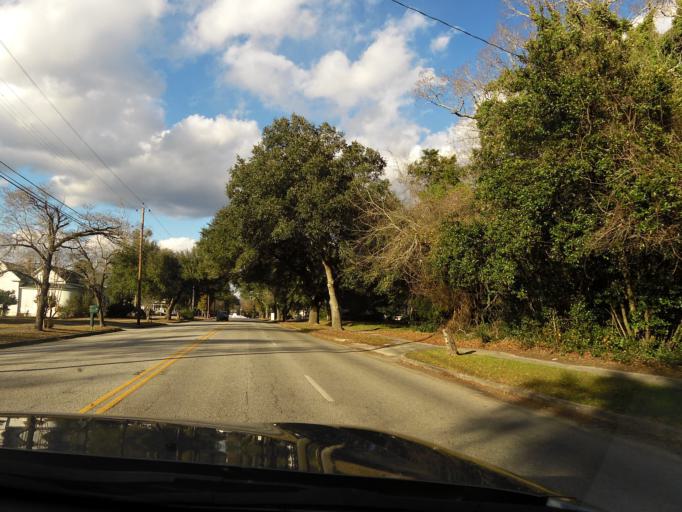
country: US
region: South Carolina
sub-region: Clarendon County
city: Manning
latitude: 33.7021
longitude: -80.2089
